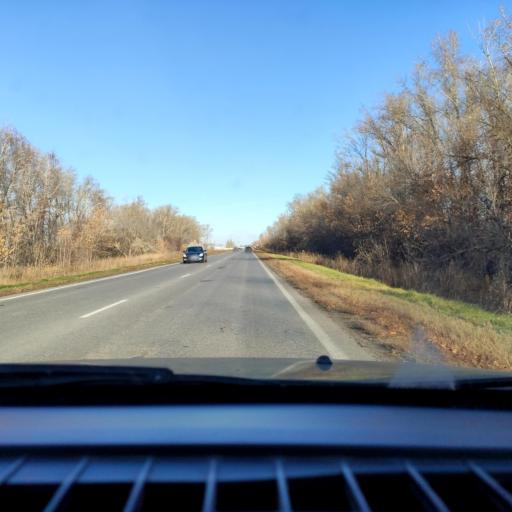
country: RU
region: Samara
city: Tol'yatti
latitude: 53.6280
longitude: 49.3048
